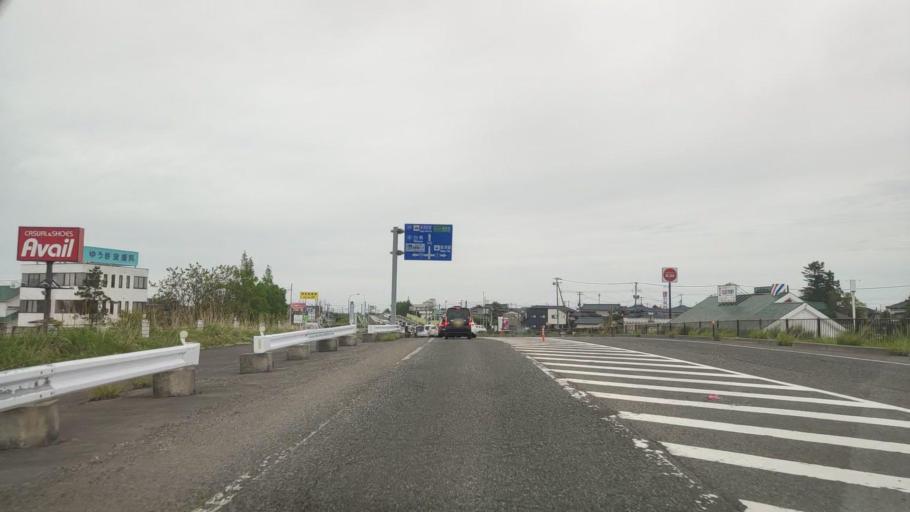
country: JP
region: Niigata
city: Niitsu-honcho
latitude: 37.7928
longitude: 139.1105
